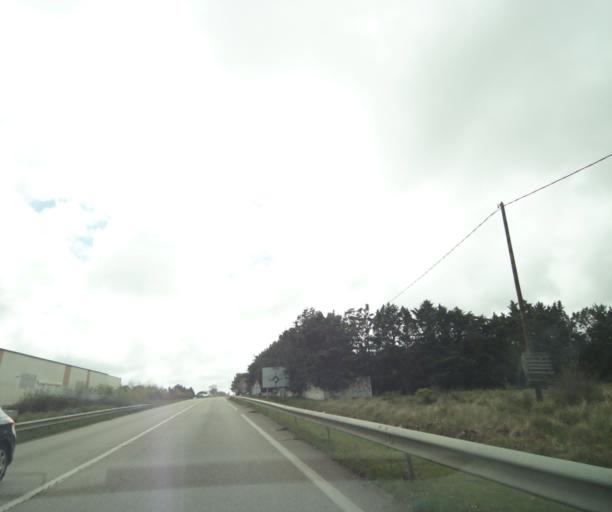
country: FR
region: Languedoc-Roussillon
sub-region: Departement de l'Herault
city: Fabregues
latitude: 43.5374
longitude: 3.7593
